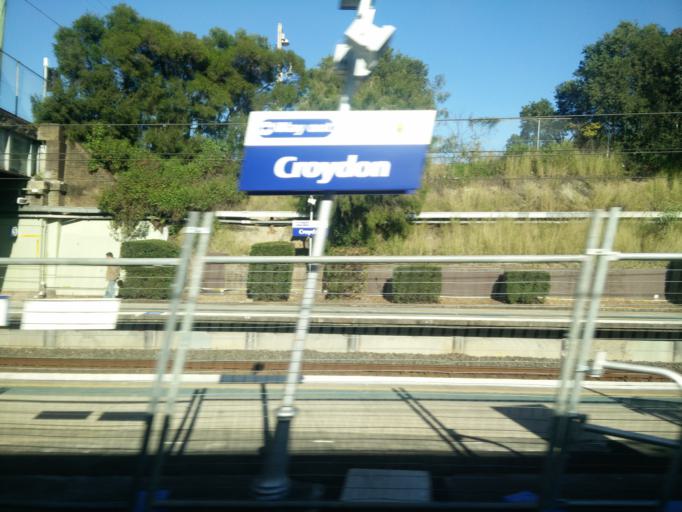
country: AU
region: New South Wales
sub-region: Ashfield
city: Croydon
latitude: -33.8829
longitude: 151.1150
